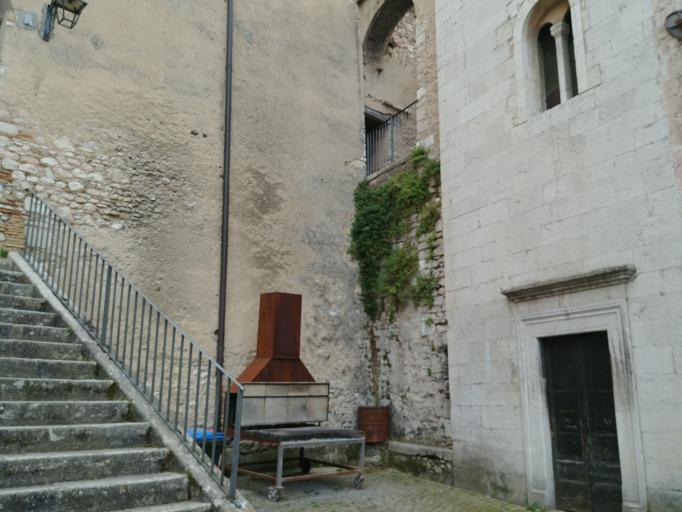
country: IT
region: Umbria
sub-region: Provincia di Terni
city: Stroncone
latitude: 42.4982
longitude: 12.6624
